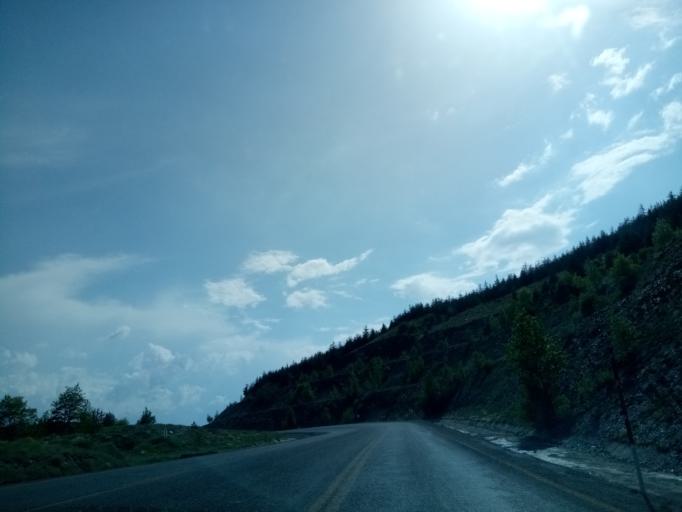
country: TR
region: Isparta
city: Bagkonak
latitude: 38.2501
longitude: 31.3377
